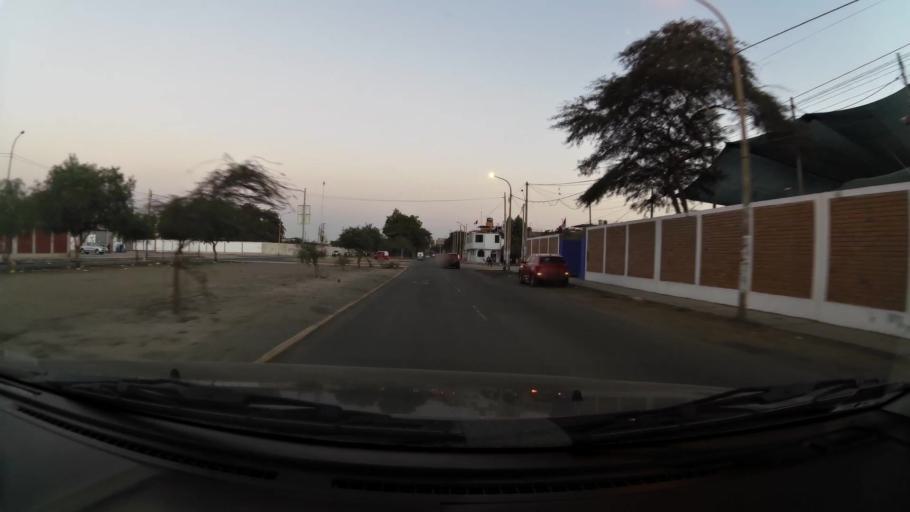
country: PE
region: Ica
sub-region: Provincia de Ica
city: Ica
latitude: -14.0776
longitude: -75.7330
